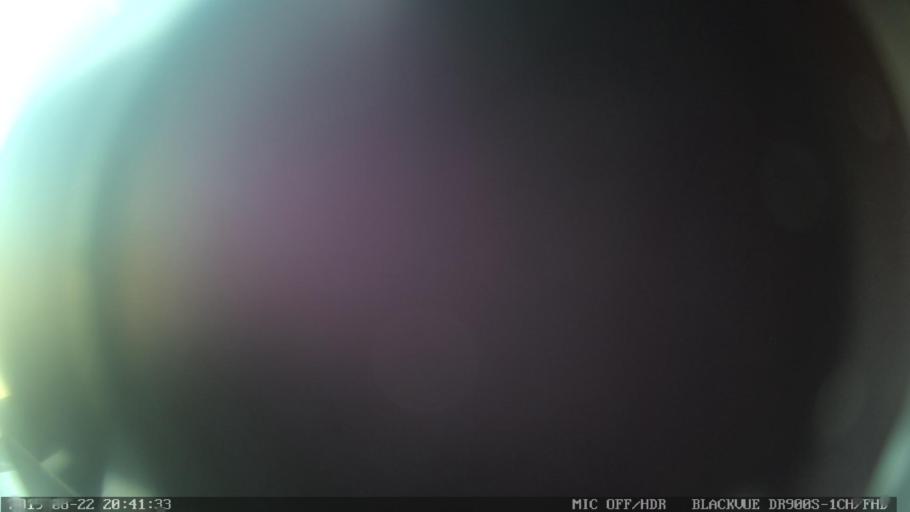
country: PT
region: Castelo Branco
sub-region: Proenca-A-Nova
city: Proenca-a-Nova
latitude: 39.6864
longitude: -7.8063
